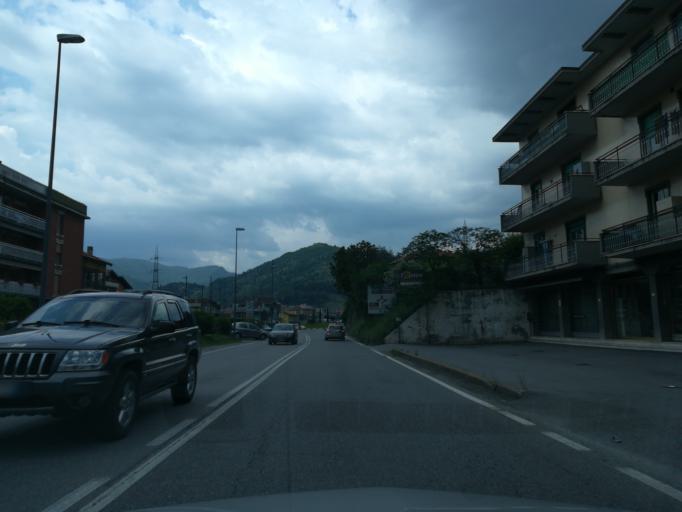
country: IT
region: Lombardy
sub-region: Provincia di Bergamo
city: Alme
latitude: 45.7410
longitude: 9.6099
